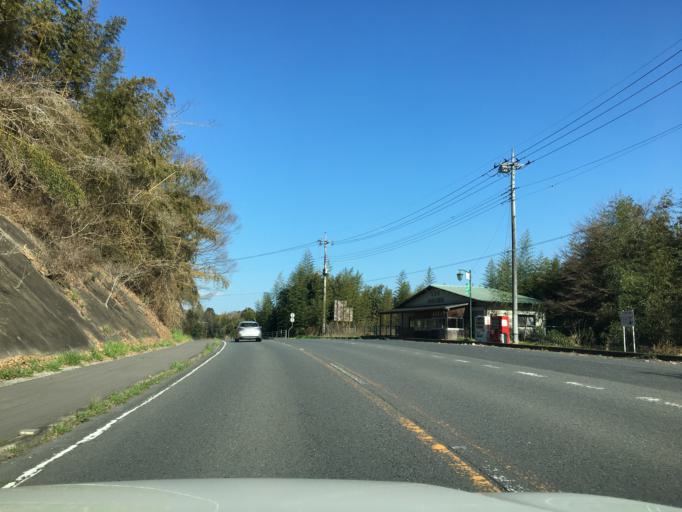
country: JP
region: Tochigi
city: Motegi
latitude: 36.5619
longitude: 140.2649
